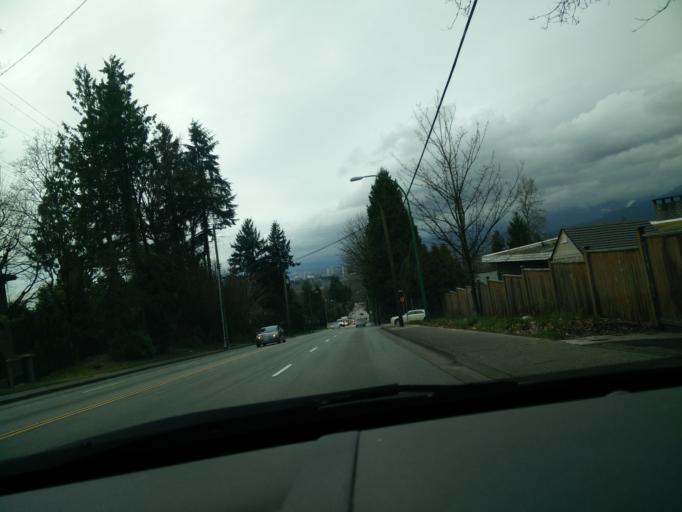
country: CA
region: British Columbia
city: Burnaby
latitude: 49.2318
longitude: -122.9501
